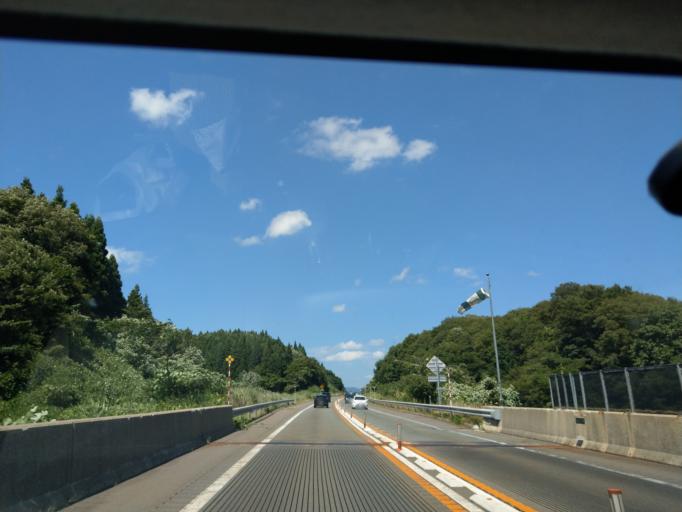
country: JP
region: Akita
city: Akita
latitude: 39.6784
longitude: 140.1857
